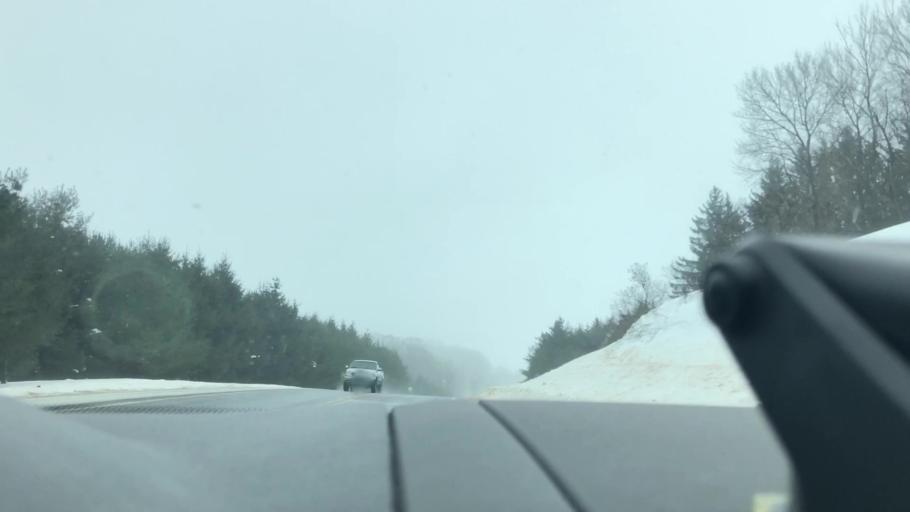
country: US
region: Michigan
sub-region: Charlevoix County
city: East Jordan
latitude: 45.1578
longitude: -85.1611
